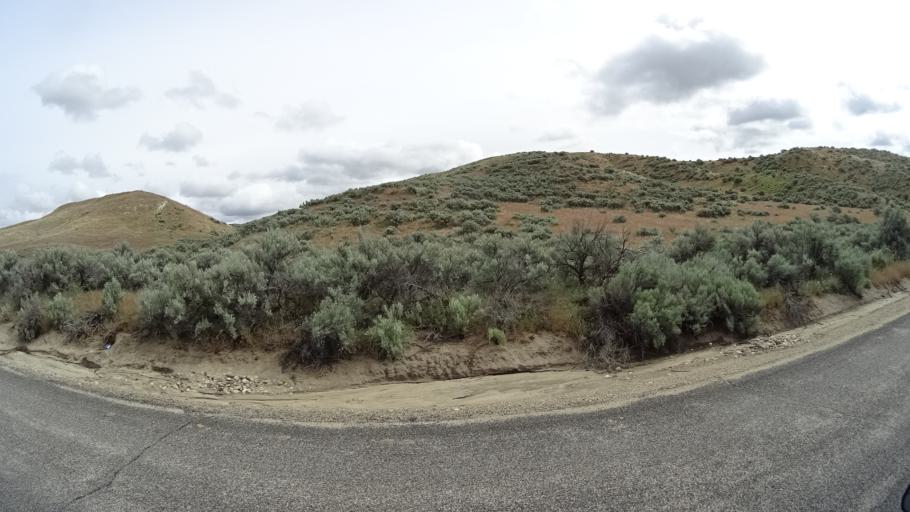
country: US
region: Idaho
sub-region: Ada County
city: Eagle
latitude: 43.7545
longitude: -116.3641
